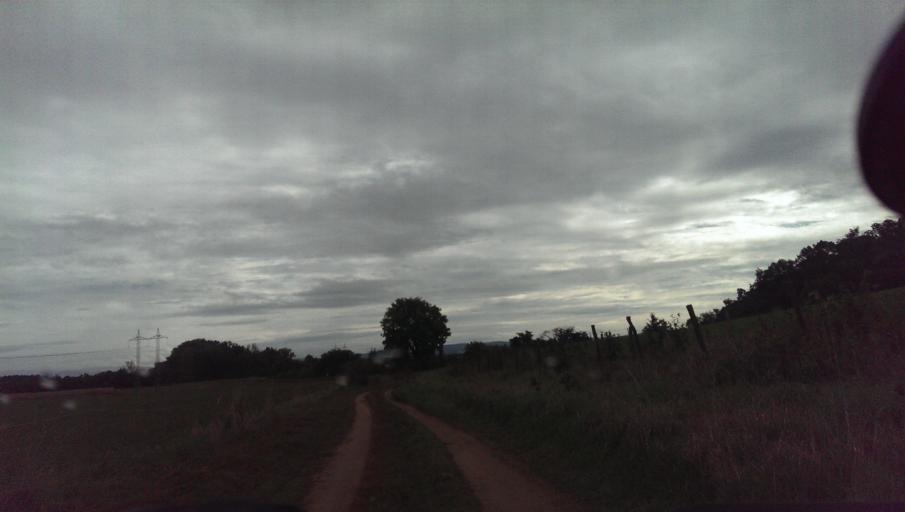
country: CZ
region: South Moravian
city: Moravsky Pisek
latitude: 48.9948
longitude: 17.3140
